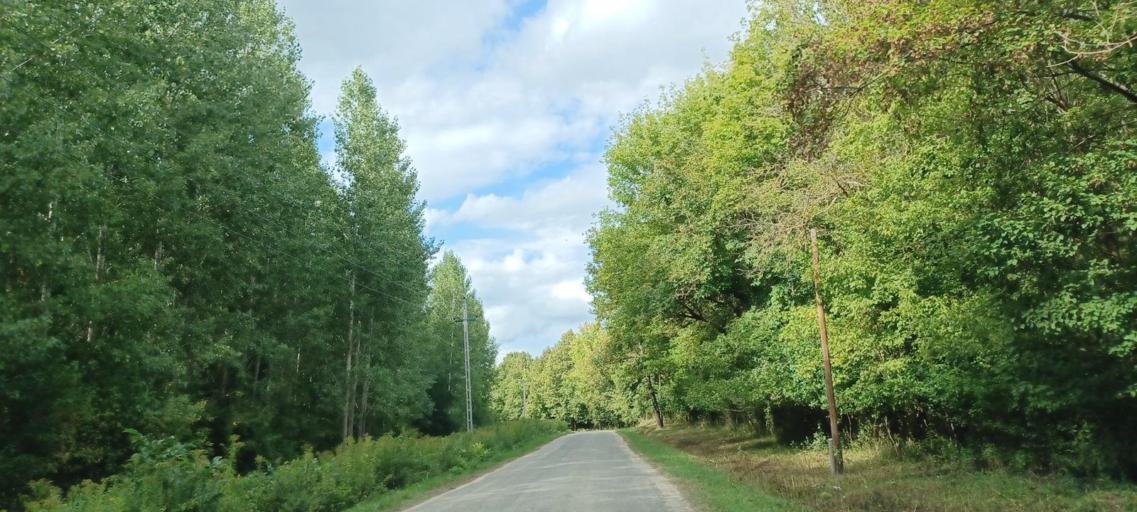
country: HU
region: Tolna
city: Szentgalpuszta
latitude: 46.3450
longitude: 18.6214
